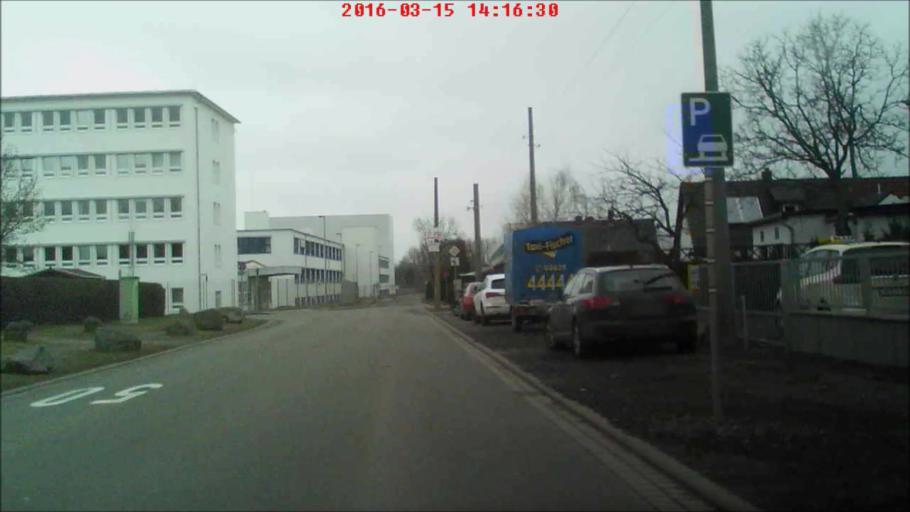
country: DE
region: Thuringia
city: Arnstadt
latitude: 50.8441
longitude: 10.9616
